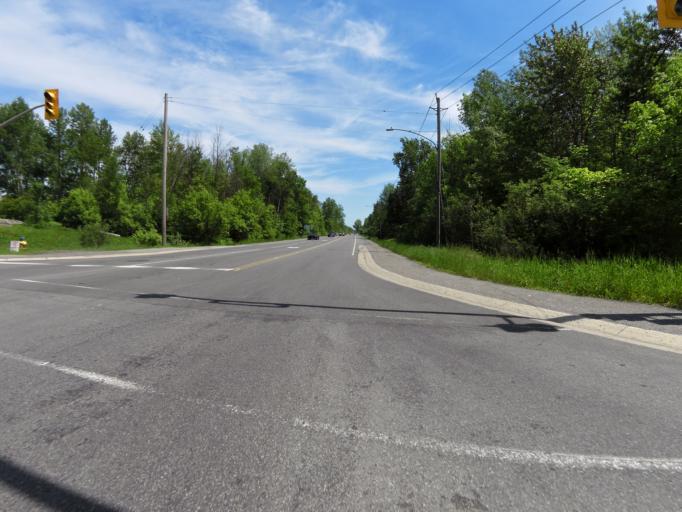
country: CA
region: Ontario
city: Ottawa
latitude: 45.3377
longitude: -75.6336
